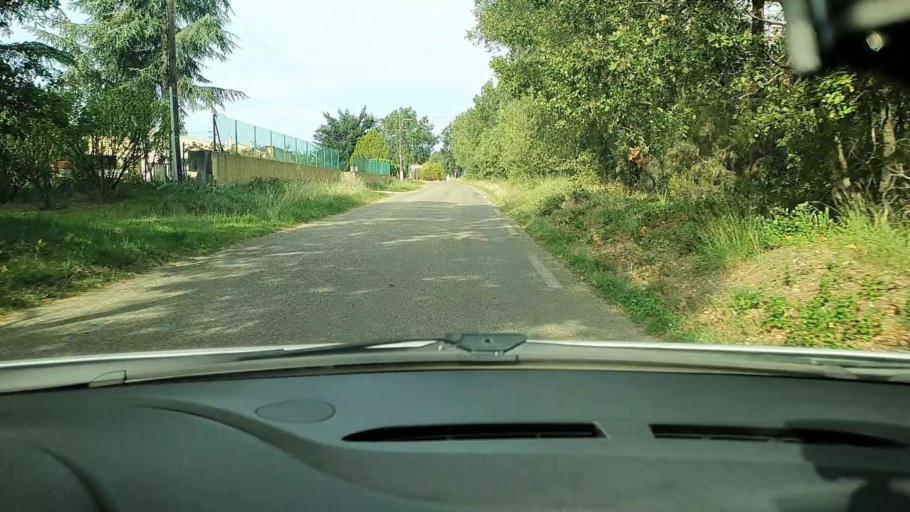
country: FR
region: Languedoc-Roussillon
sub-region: Departement du Gard
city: Saint-Quentin-la-Poterie
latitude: 44.1090
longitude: 4.4211
